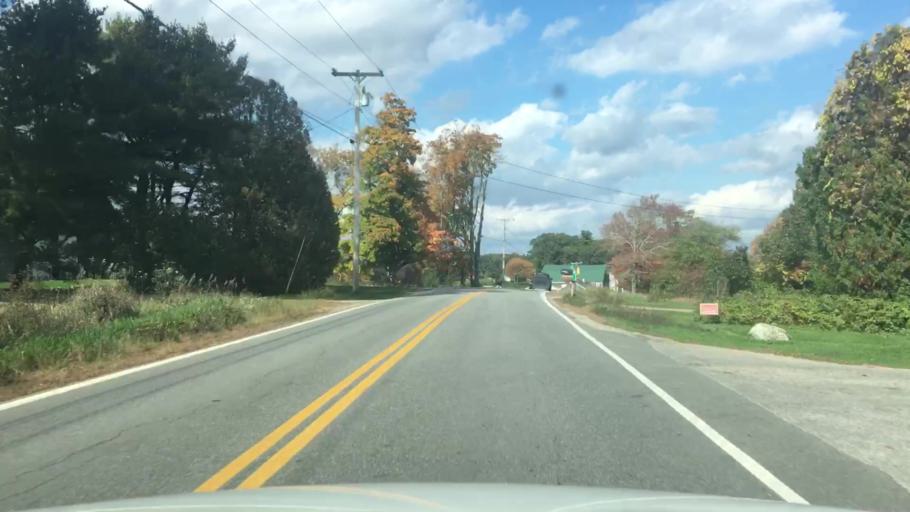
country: US
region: Maine
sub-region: Knox County
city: Appleton
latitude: 44.2584
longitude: -69.2765
